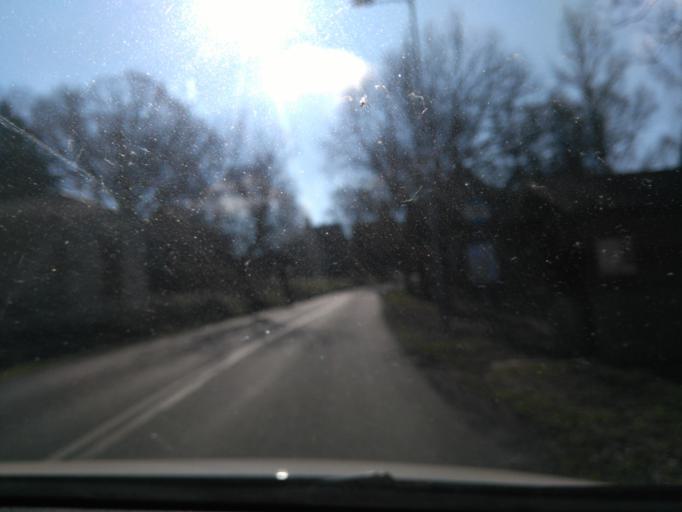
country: CZ
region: Ustecky
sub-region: Okres Chomutov
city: Vejprty
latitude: 50.4932
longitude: 13.0369
